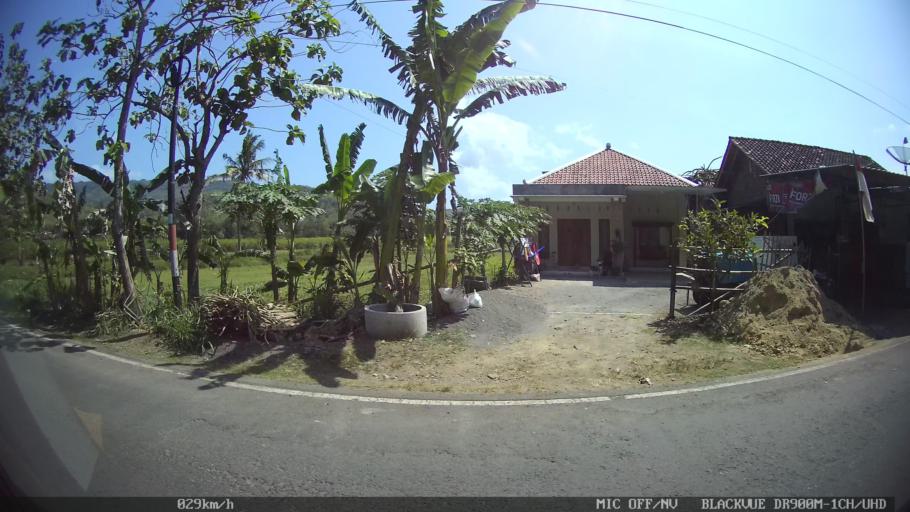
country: ID
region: Daerah Istimewa Yogyakarta
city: Pundong
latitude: -7.9540
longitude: 110.3795
